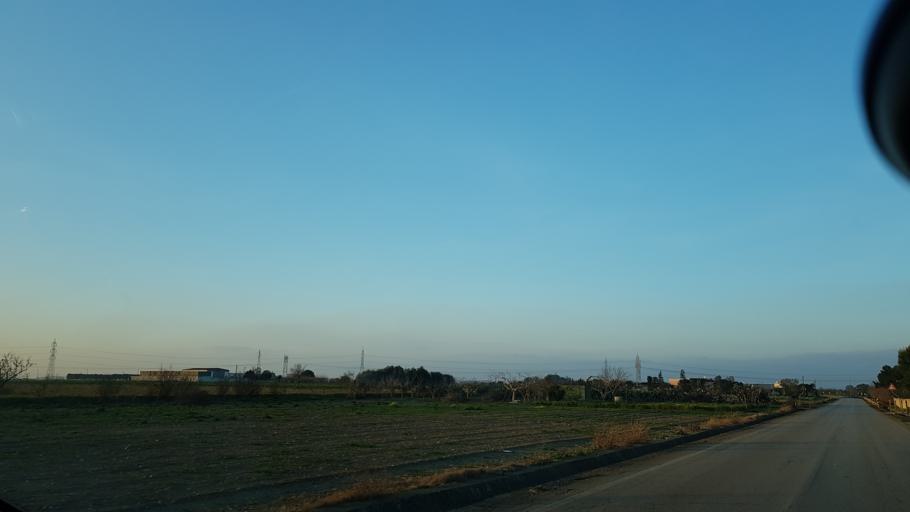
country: IT
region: Apulia
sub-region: Provincia di Brindisi
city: La Rosa
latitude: 40.5942
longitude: 17.9457
